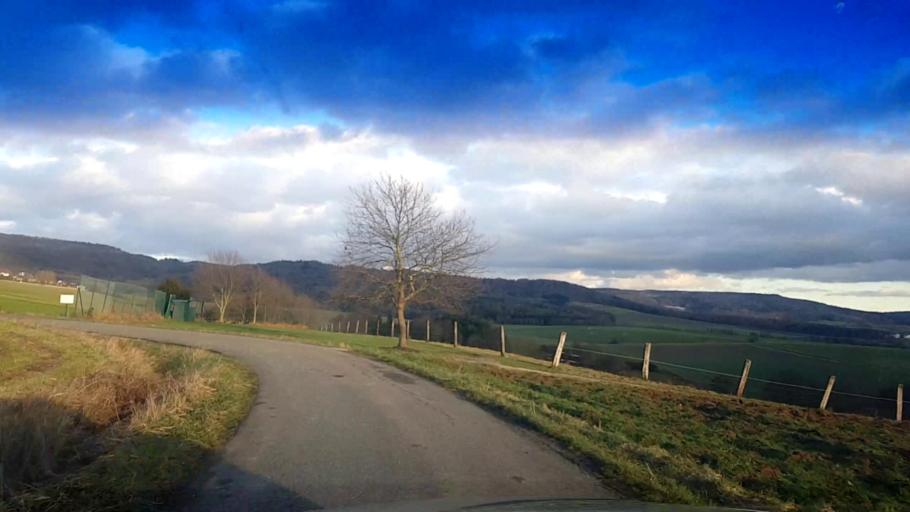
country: DE
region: Bavaria
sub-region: Upper Franconia
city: Buttenheim
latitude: 49.8165
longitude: 11.0409
